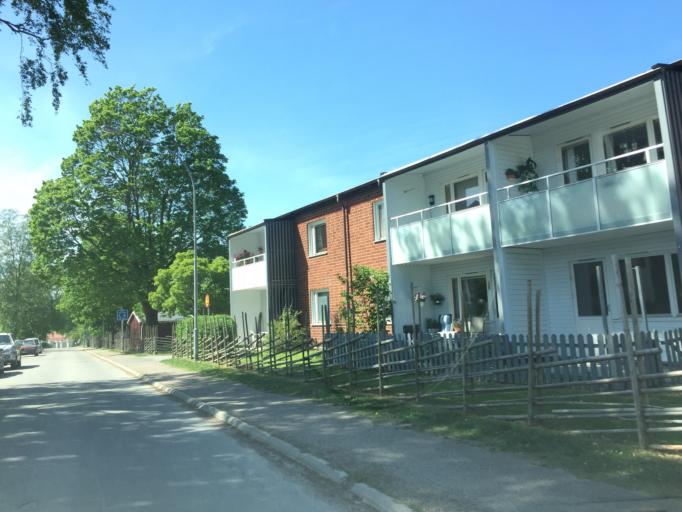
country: SE
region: OErebro
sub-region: Orebro Kommun
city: Orebro
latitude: 59.2651
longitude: 15.2524
